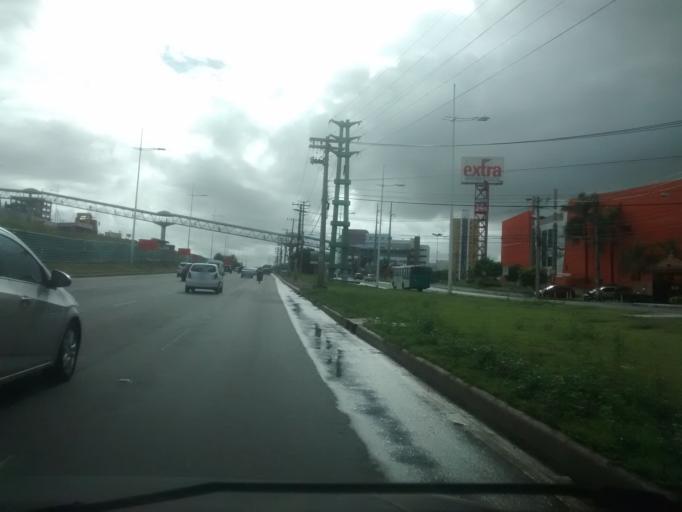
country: BR
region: Bahia
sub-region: Salvador
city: Salvador
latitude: -12.9637
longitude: -38.4350
